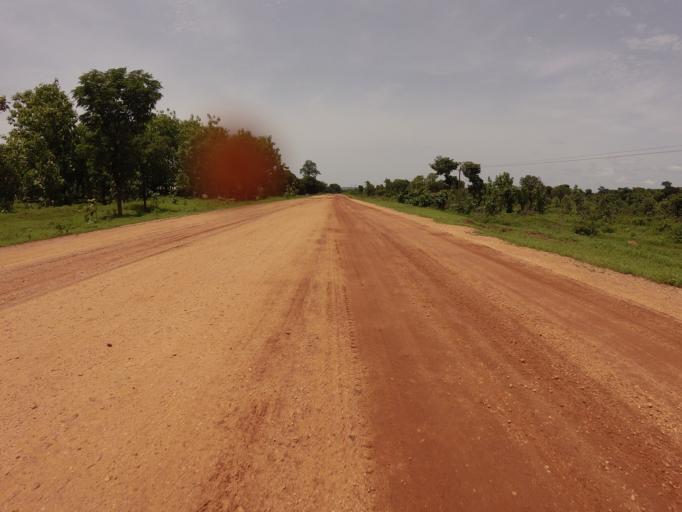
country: GH
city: Kpandae
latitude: 8.7203
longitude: 0.1339
